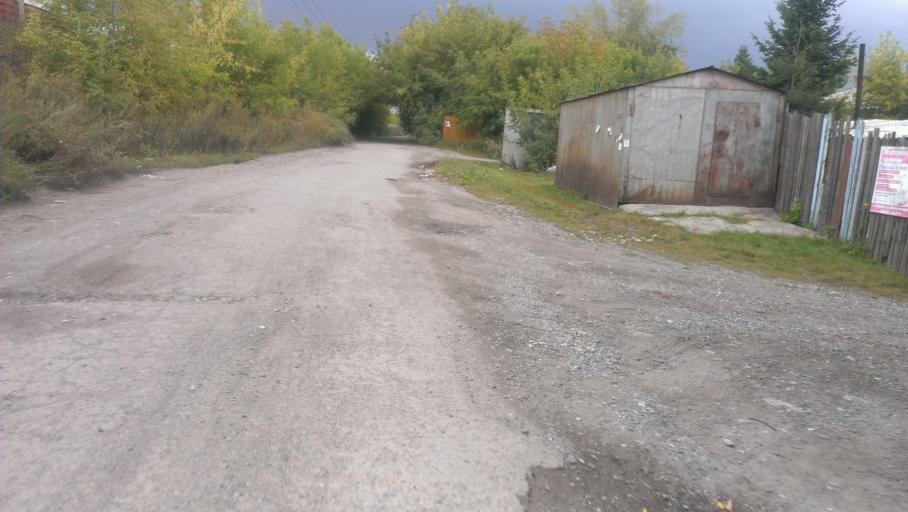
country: RU
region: Altai Krai
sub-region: Gorod Barnaulskiy
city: Barnaul
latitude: 53.3492
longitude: 83.7522
